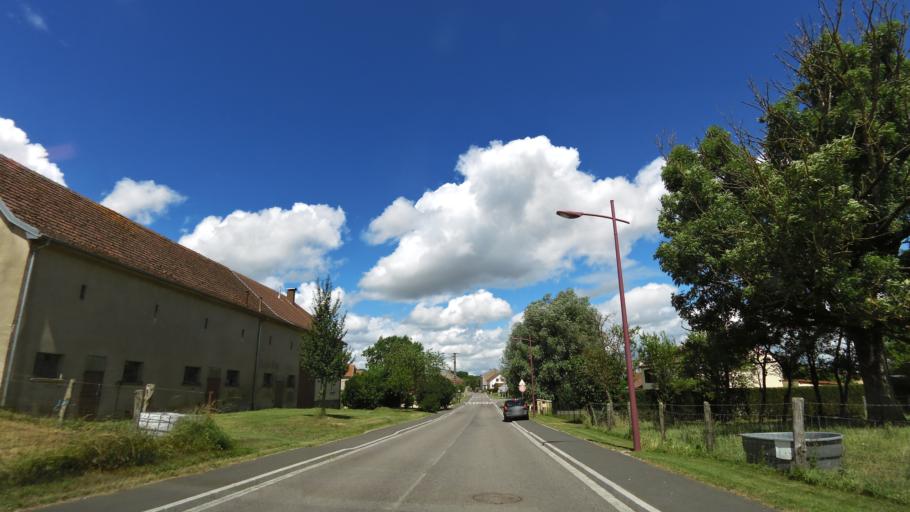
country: FR
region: Lorraine
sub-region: Departement de la Moselle
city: Lorquin
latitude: 48.6282
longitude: 6.9674
